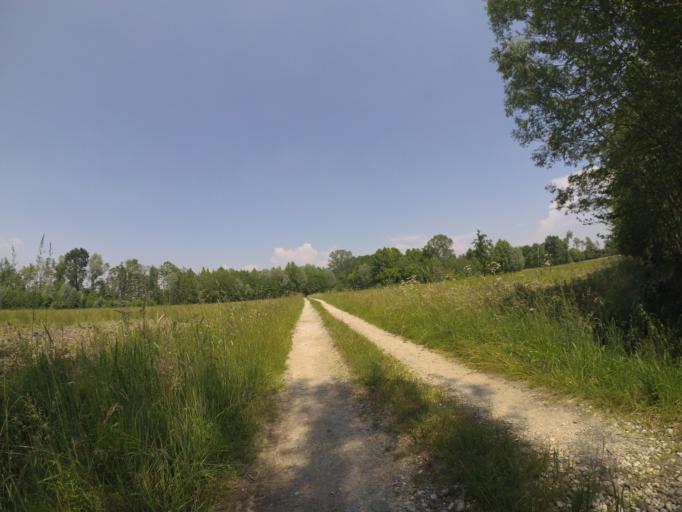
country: IT
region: Friuli Venezia Giulia
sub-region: Provincia di Udine
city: Bertiolo
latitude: 45.9154
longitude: 13.0340
